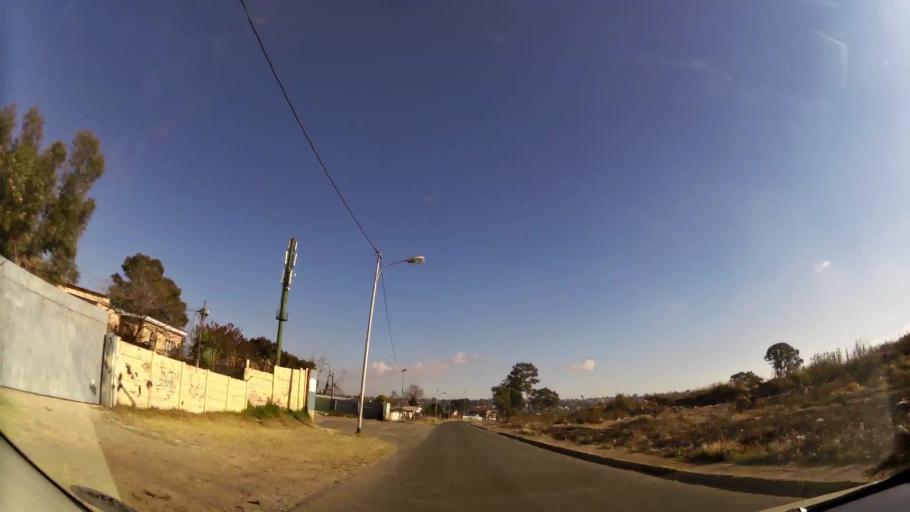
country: ZA
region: Gauteng
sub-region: City of Johannesburg Metropolitan Municipality
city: Roodepoort
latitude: -26.1561
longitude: 27.8559
